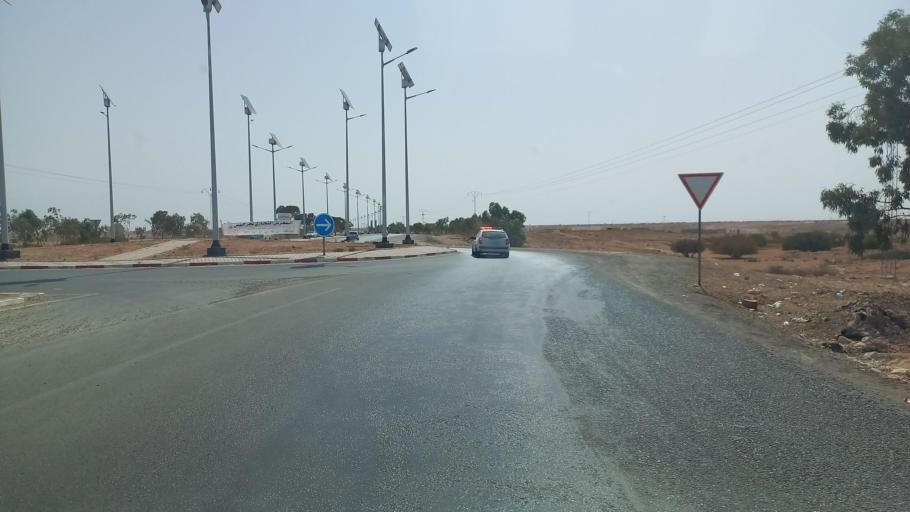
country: TN
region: Madanin
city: Medenine
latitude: 33.3605
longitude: 10.5607
